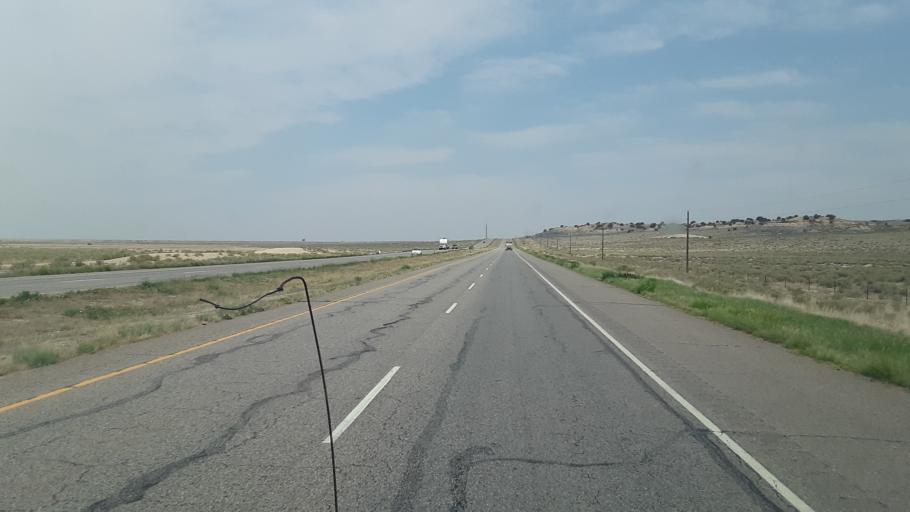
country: US
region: Colorado
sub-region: Pueblo County
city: Pueblo West
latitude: 38.3491
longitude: -104.8063
